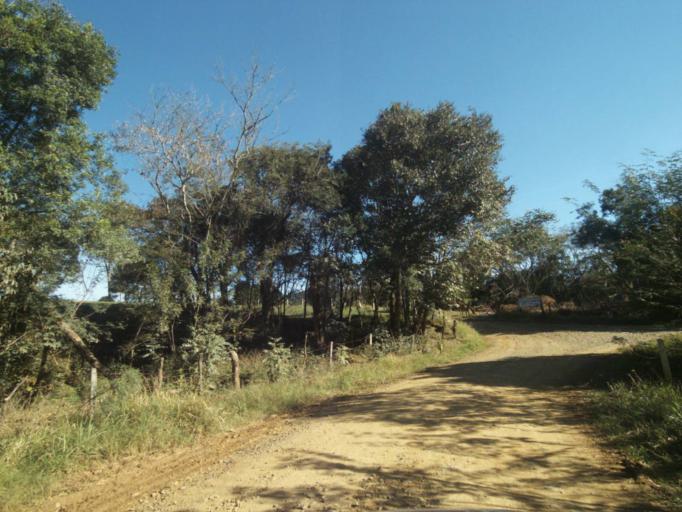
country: BR
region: Parana
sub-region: Tibagi
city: Tibagi
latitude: -24.5513
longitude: -50.5182
